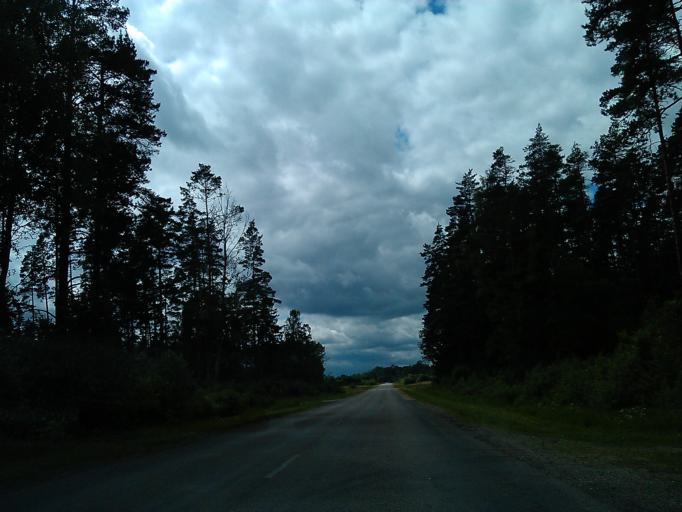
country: LV
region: Talsu Rajons
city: Stende
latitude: 57.0826
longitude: 22.2993
